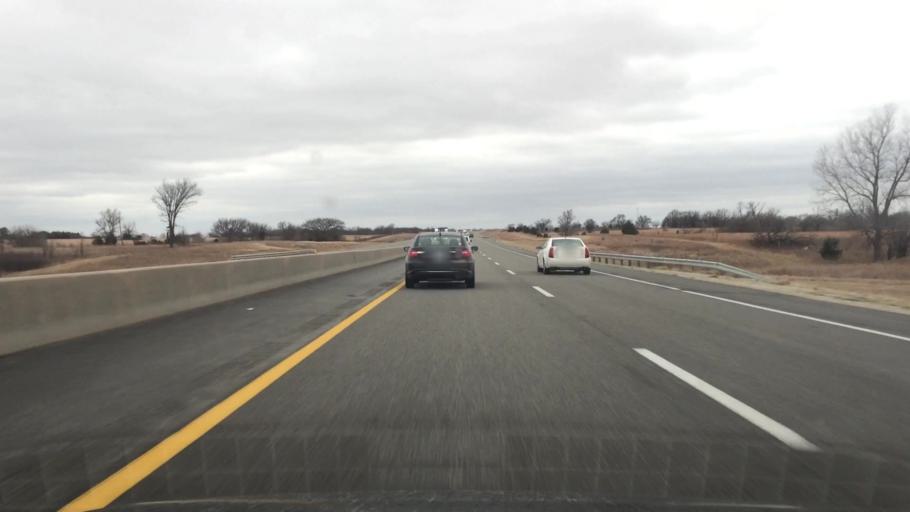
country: US
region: Kansas
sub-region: Butler County
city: Towanda
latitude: 37.7917
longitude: -96.9375
